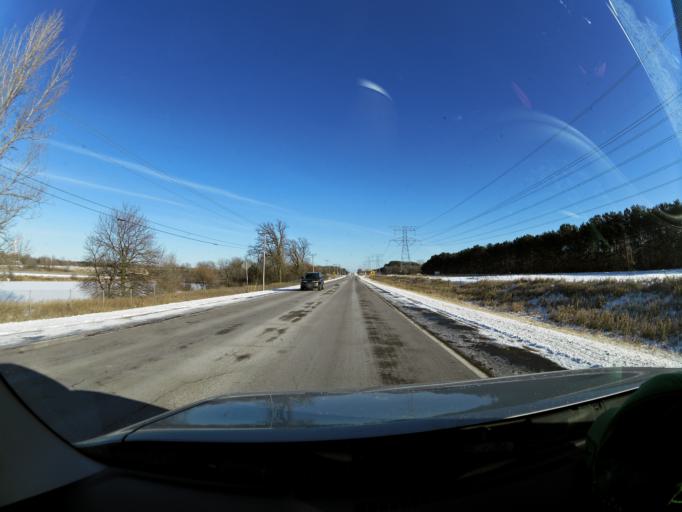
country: US
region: Minnesota
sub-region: Washington County
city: Lake Elmo
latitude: 44.9469
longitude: -92.8471
